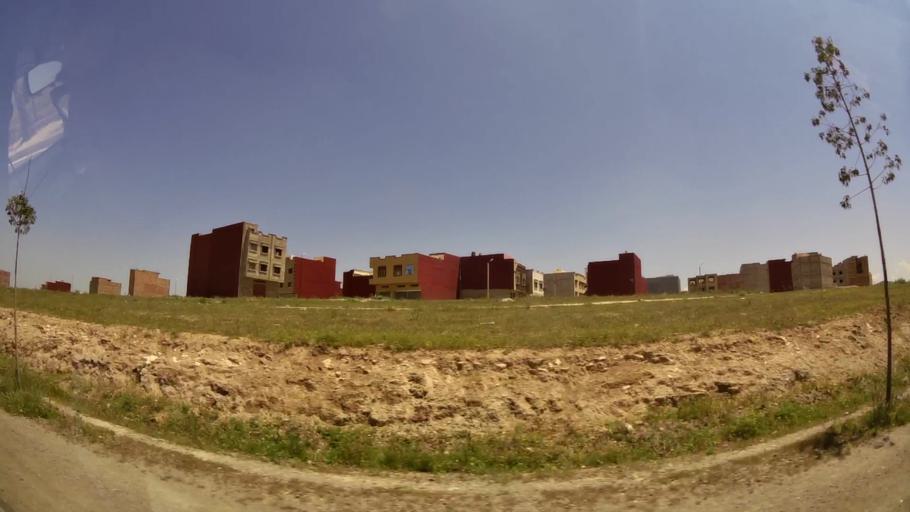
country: MA
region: Oriental
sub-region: Oujda-Angad
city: Oujda
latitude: 34.6598
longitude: -1.9550
